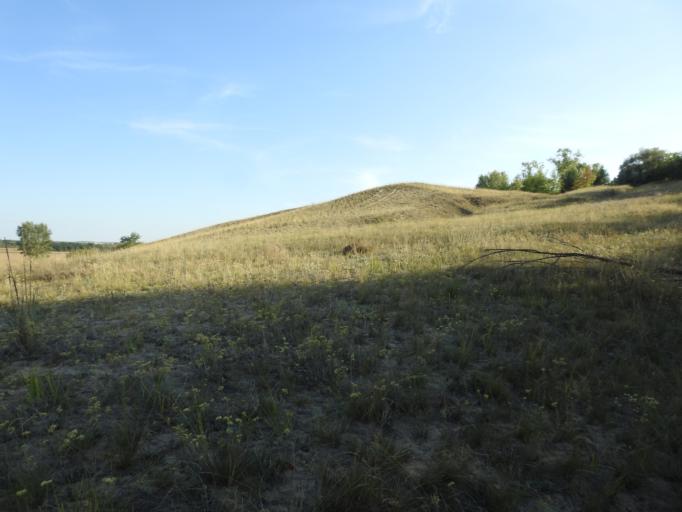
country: RU
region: Volgograd
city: Zhirnovsk
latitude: 51.1915
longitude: 44.9442
